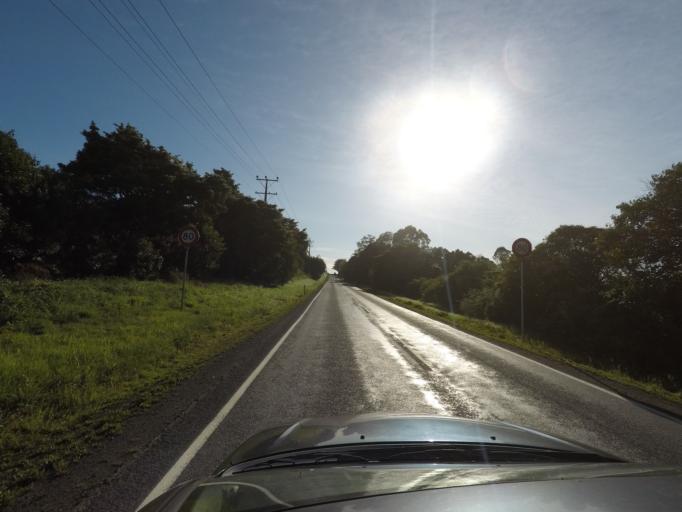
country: NZ
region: Auckland
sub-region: Auckland
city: Red Hill
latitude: -37.0150
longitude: 174.9437
